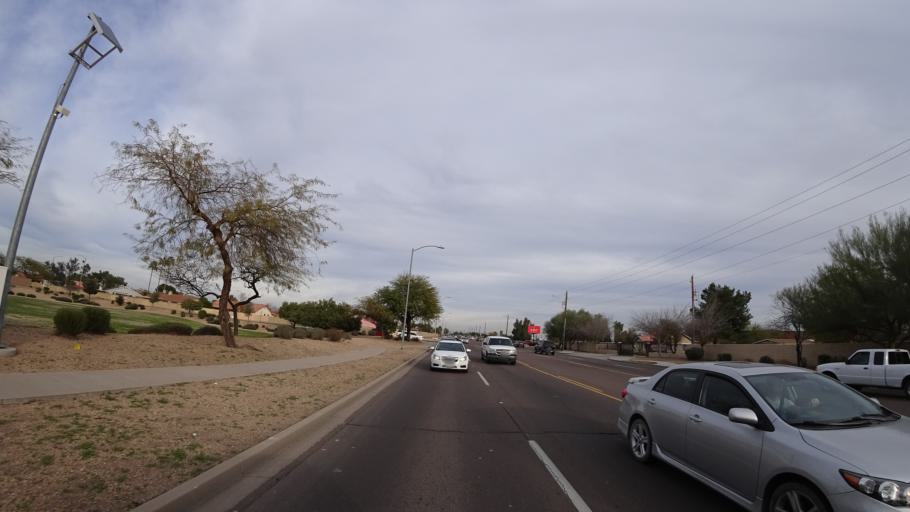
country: US
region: Arizona
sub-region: Maricopa County
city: Peoria
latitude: 33.5665
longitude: -112.2429
